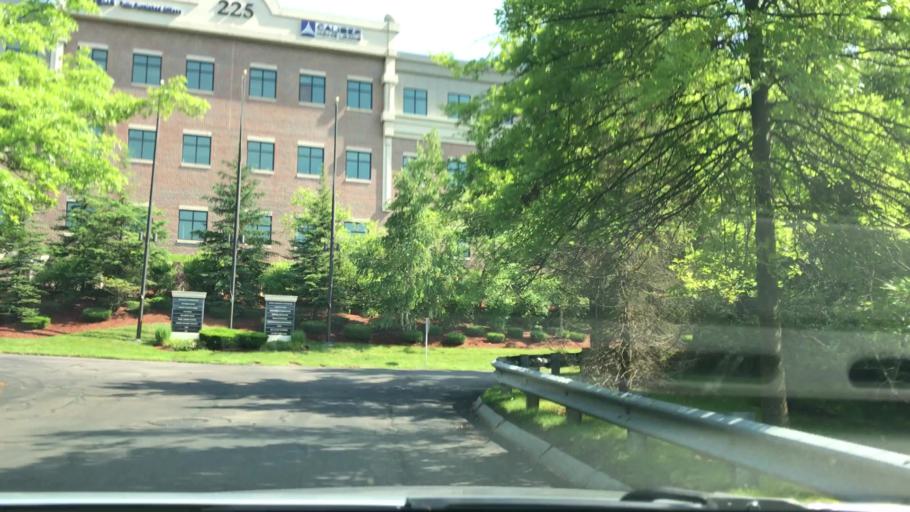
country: US
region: Massachusetts
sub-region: Middlesex County
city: Marlborough
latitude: 42.3198
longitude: -71.5860
